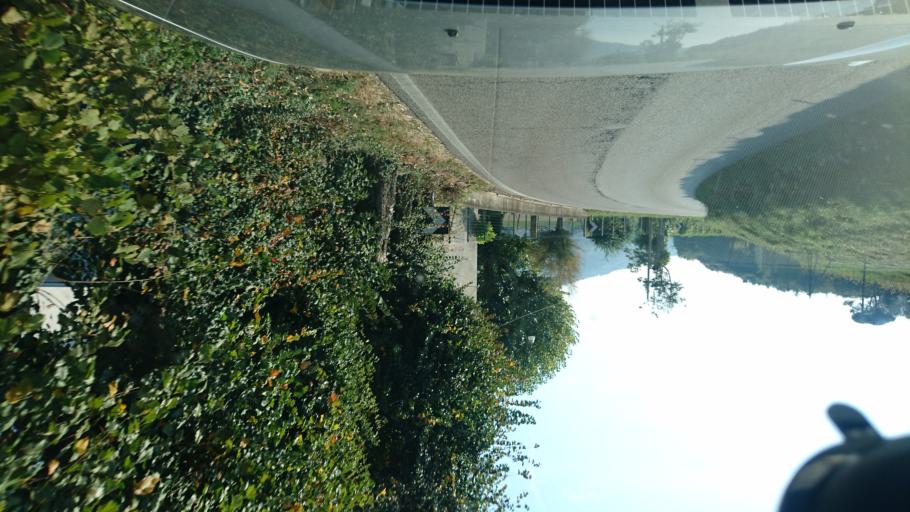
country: IT
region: Veneto
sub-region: Provincia di Vicenza
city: Longare
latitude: 45.4956
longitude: 11.6045
